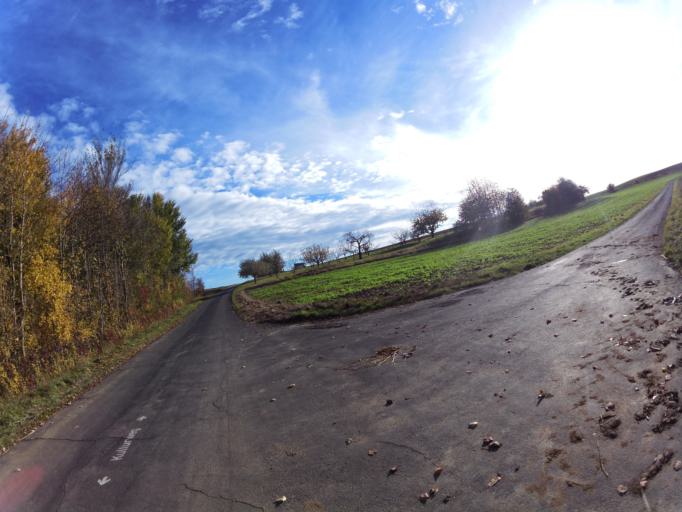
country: DE
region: Bavaria
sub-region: Regierungsbezirk Unterfranken
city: Giebelstadt
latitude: 49.6679
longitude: 9.9592
